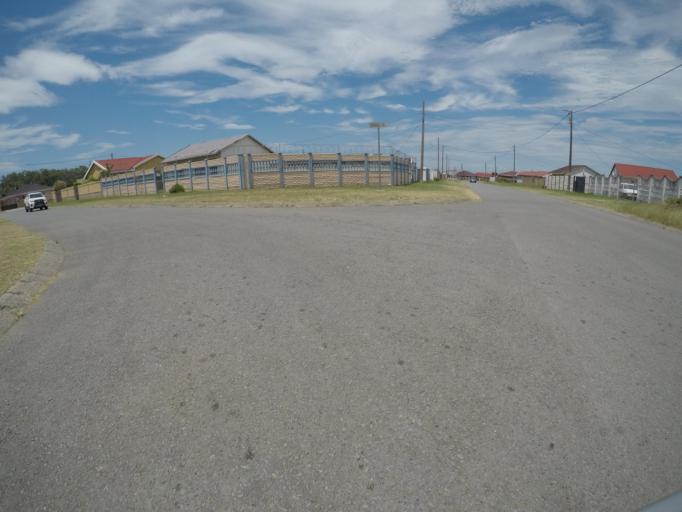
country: ZA
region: Eastern Cape
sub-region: Buffalo City Metropolitan Municipality
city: East London
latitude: -33.0463
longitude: 27.8494
